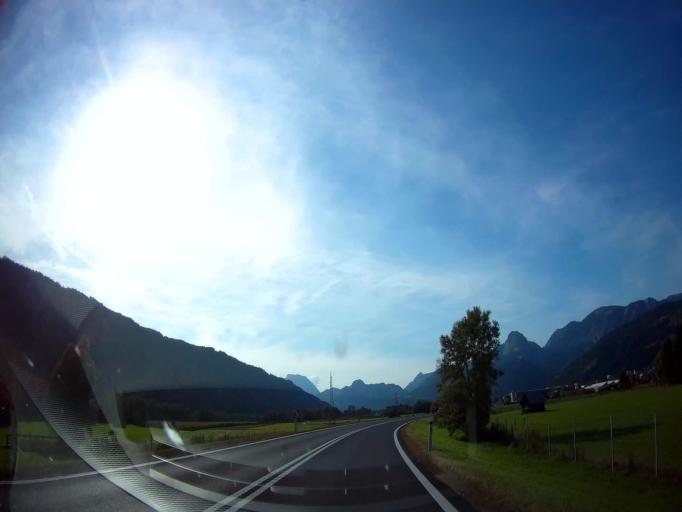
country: AT
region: Styria
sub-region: Politischer Bezirk Liezen
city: Liezen
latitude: 47.5543
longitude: 14.2630
